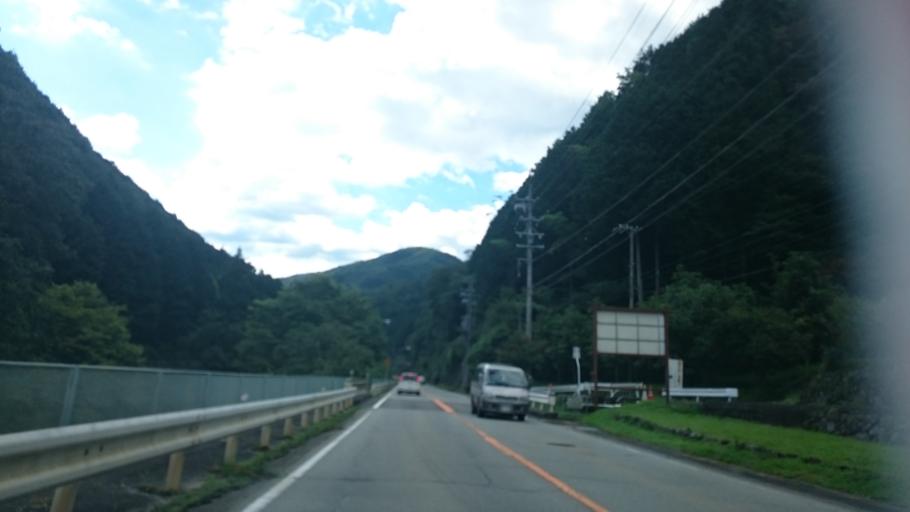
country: JP
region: Gifu
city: Gujo
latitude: 35.7691
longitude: 137.2811
